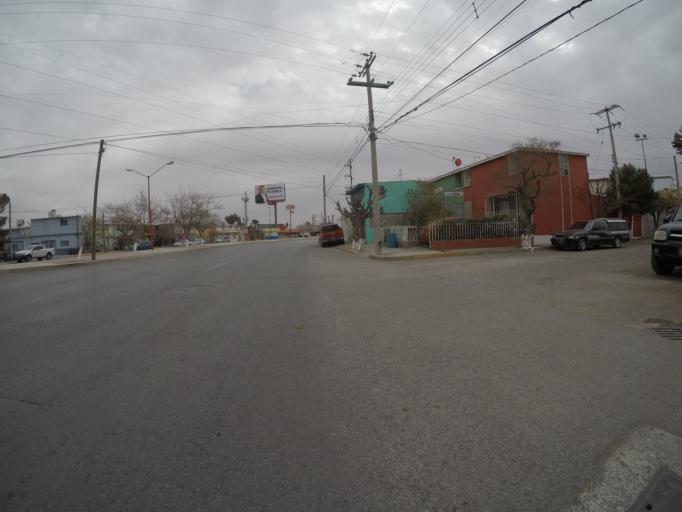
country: MX
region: Chihuahua
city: Ciudad Juarez
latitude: 31.7366
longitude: -106.4178
